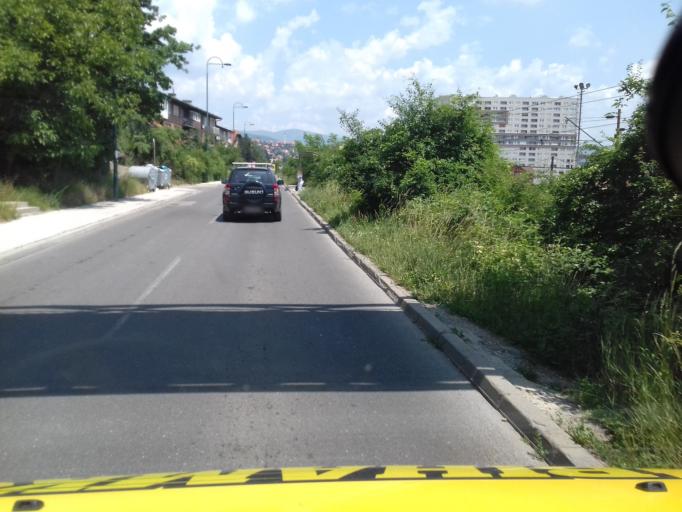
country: BA
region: Federation of Bosnia and Herzegovina
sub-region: Kanton Sarajevo
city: Sarajevo
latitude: 43.8564
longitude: 18.3779
